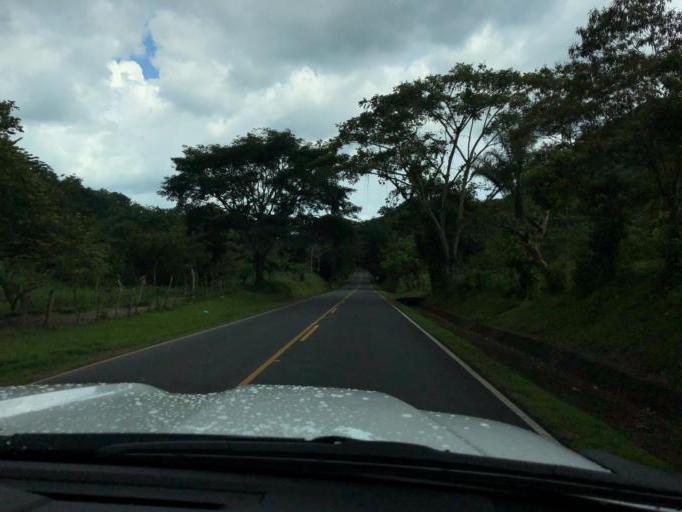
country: NI
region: Chontales
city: Villa Sandino
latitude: 11.9983
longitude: -84.8881
